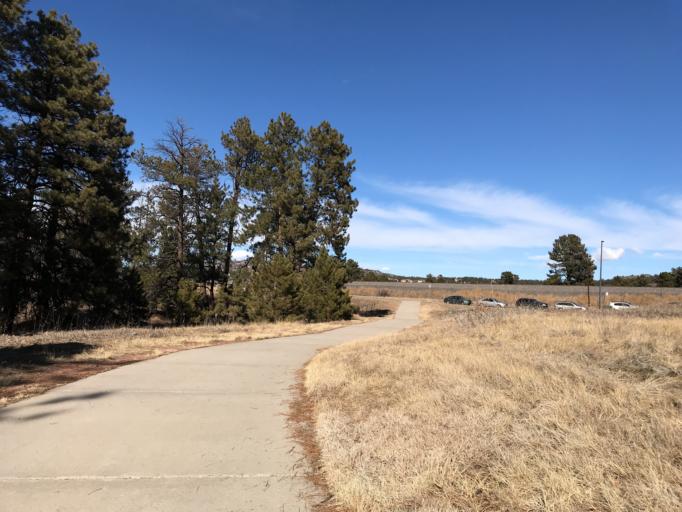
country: US
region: Colorado
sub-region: Douglas County
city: Castle Pines
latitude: 39.4110
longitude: -104.8902
